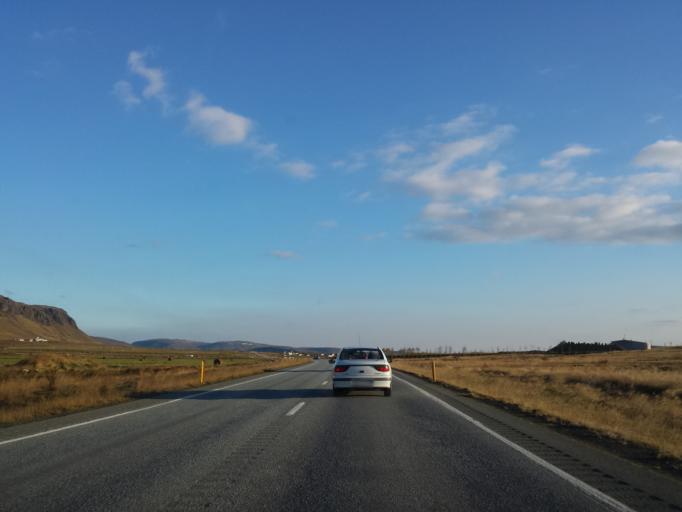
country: IS
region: Capital Region
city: Mosfellsbaer
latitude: 64.2220
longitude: -21.8061
